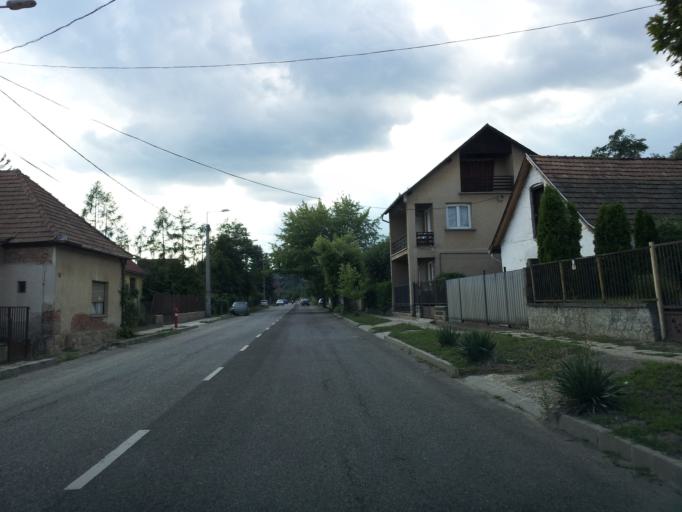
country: HU
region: Pest
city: Kismaros
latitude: 47.8266
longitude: 19.0038
